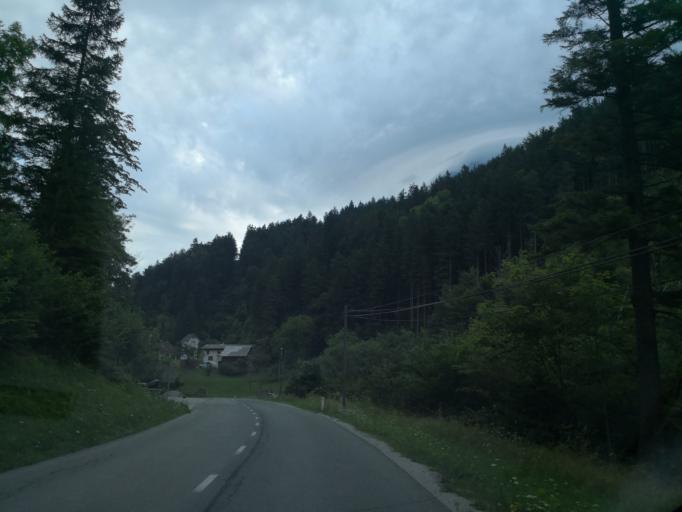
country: SI
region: Cerklje na Gorenjskem
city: Cerklje na Gorenjskem
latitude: 46.3230
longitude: 14.4957
